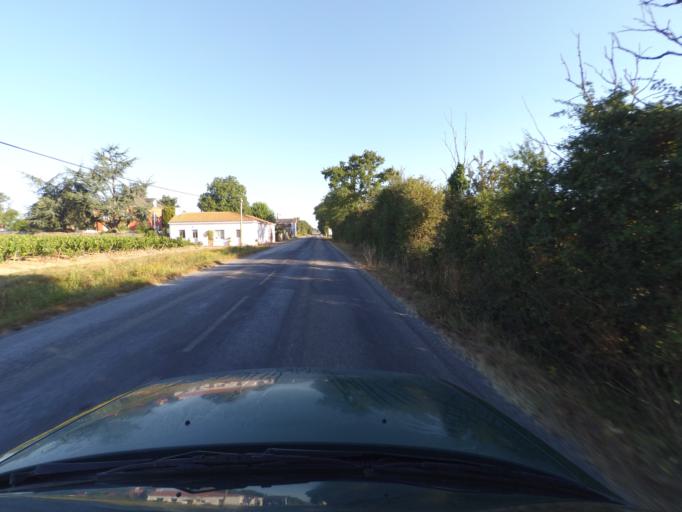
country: FR
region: Pays de la Loire
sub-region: Departement de la Loire-Atlantique
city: Vieillevigne
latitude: 46.9844
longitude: -1.4432
